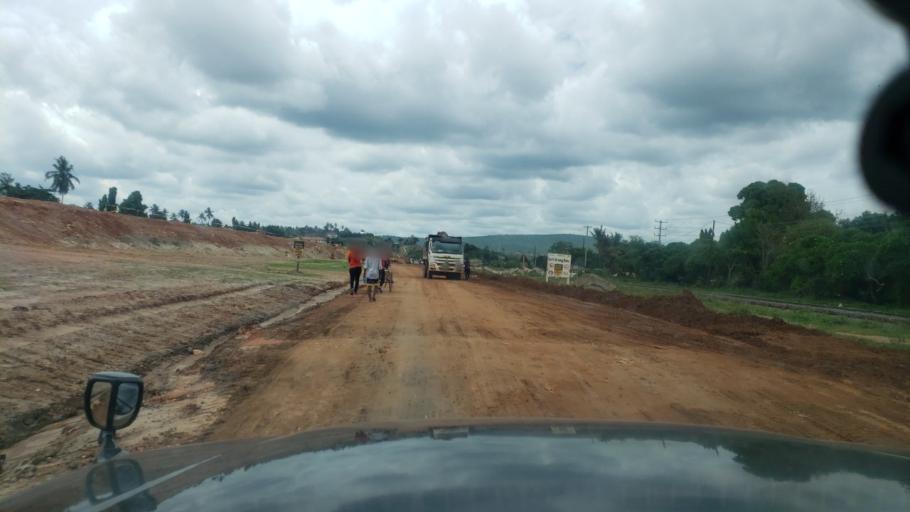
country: TZ
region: Pwani
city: Kisarawe
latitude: -6.8854
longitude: 39.1437
